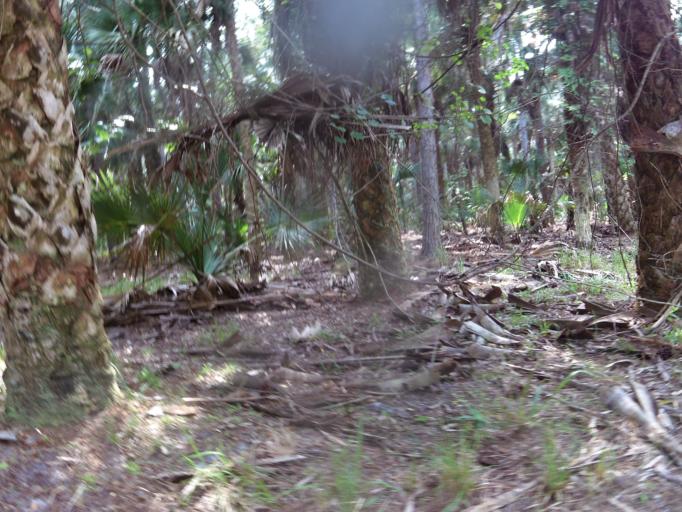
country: US
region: Florida
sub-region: Flagler County
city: Flagler Beach
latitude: 29.4022
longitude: -81.1220
